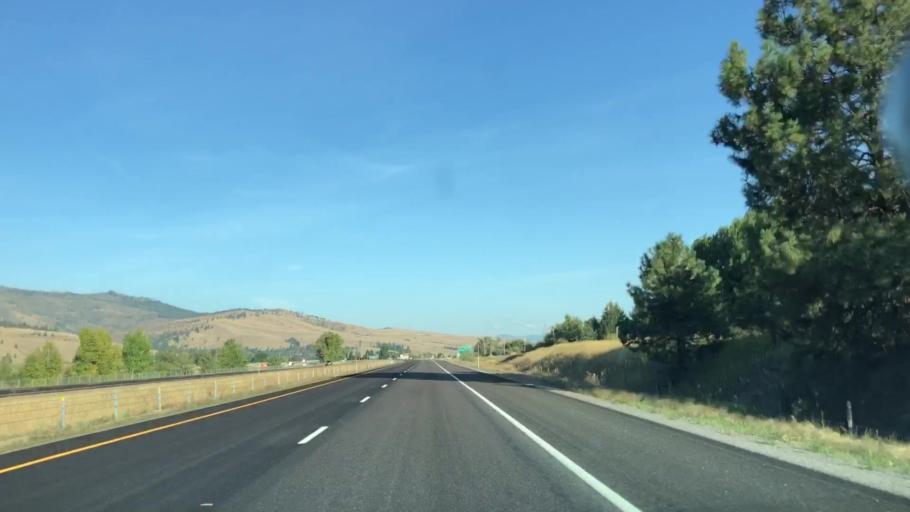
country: US
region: Montana
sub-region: Missoula County
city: Frenchtown
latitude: 47.0232
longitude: -114.2604
